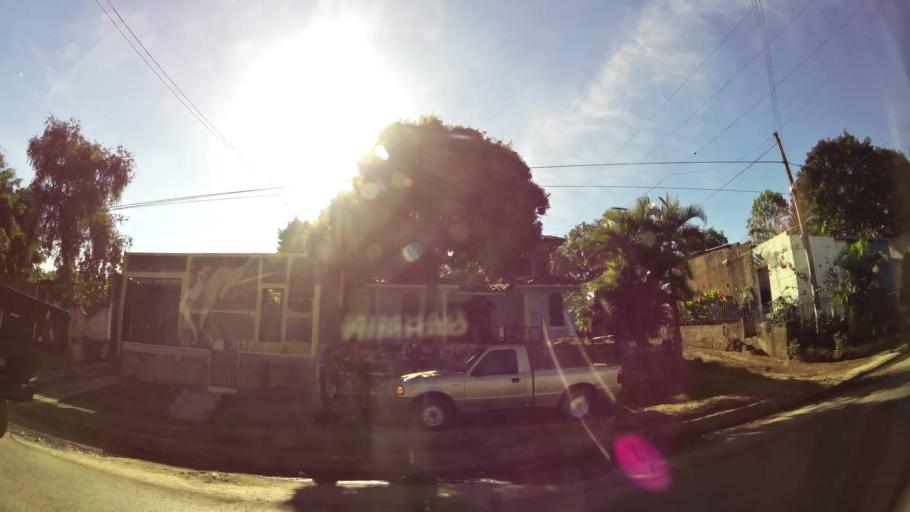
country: SV
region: Santa Ana
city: Santa Ana
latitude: 13.9752
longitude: -89.5836
